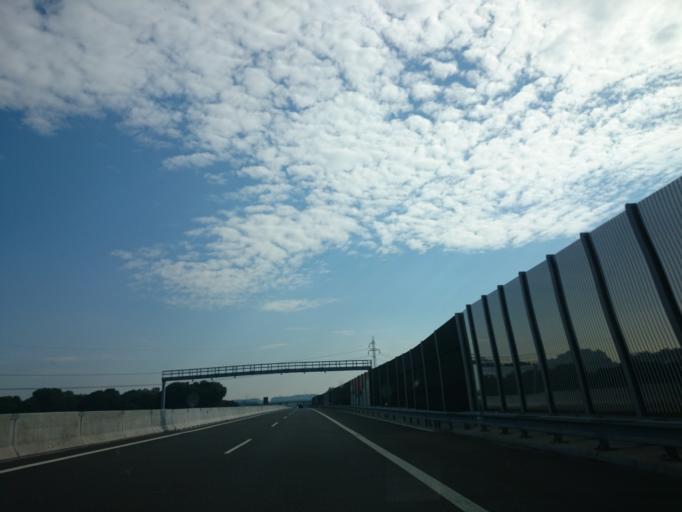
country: CZ
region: Moravskoslezsky
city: Bohumin
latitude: 49.9200
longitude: 18.3711
